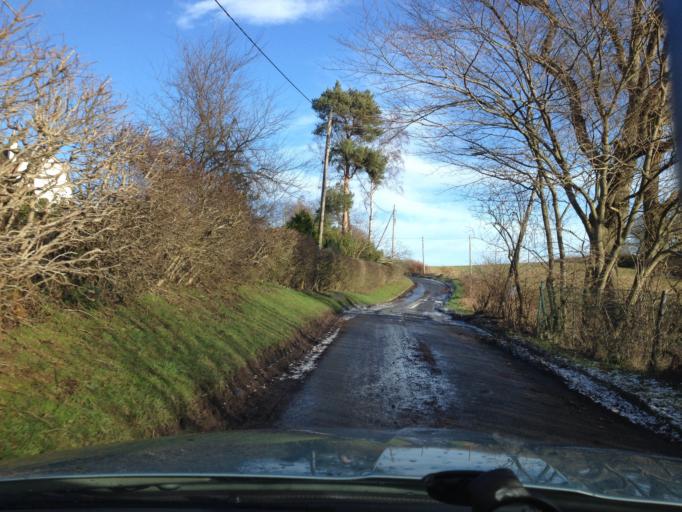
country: GB
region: Scotland
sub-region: Perth and Kinross
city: Perth
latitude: 56.3647
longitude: -3.4374
